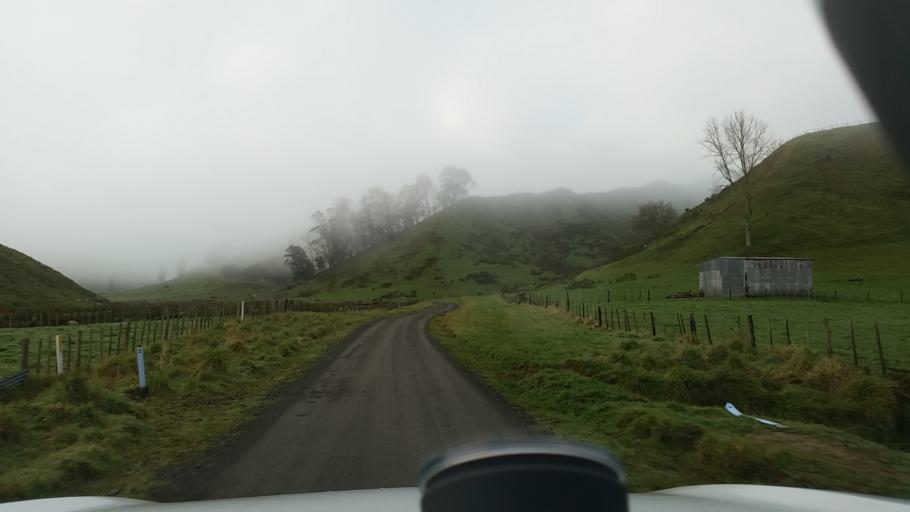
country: NZ
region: Taranaki
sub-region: South Taranaki District
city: Eltham
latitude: -39.4305
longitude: 174.4408
